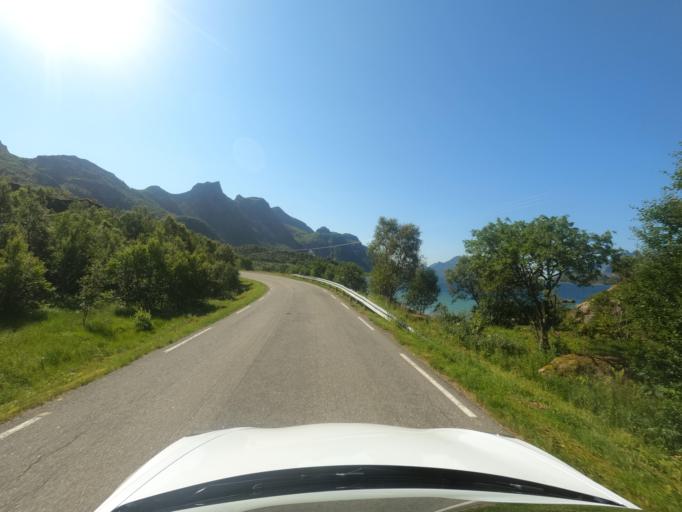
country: NO
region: Nordland
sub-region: Hadsel
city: Stokmarknes
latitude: 68.3581
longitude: 15.0634
